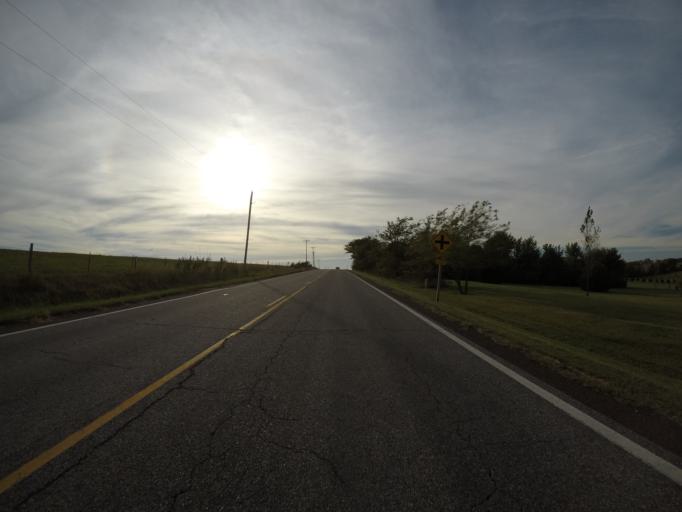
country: US
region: Kansas
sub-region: Douglas County
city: Baldwin City
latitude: 38.7823
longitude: -95.2396
